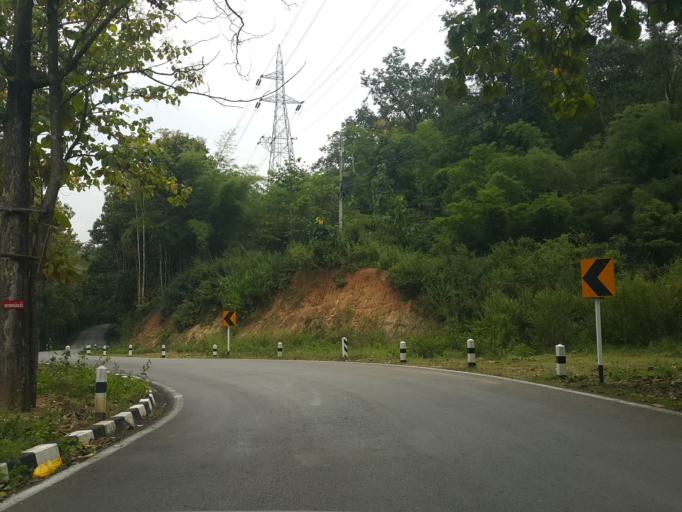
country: TH
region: Mae Hong Son
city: Mae Hi
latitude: 19.2817
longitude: 98.4891
